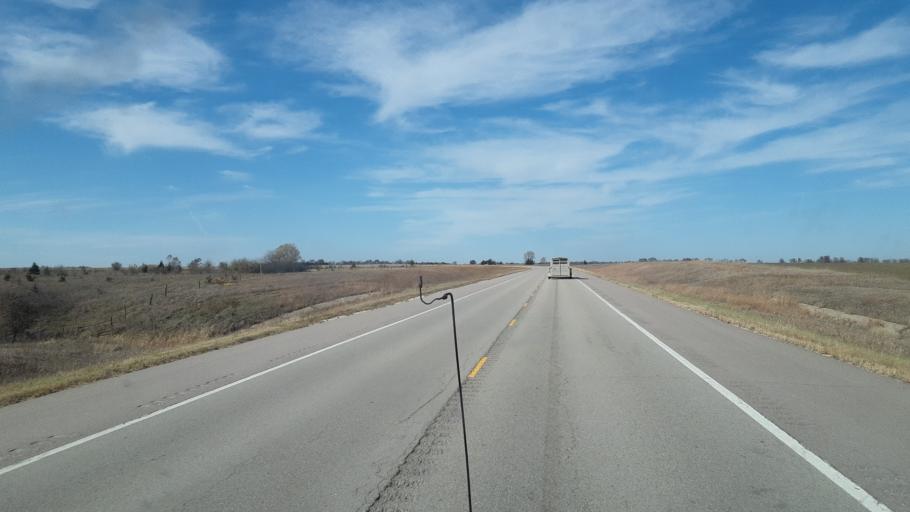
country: US
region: Kansas
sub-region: Marion County
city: Hillsboro
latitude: 38.3720
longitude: -97.3659
